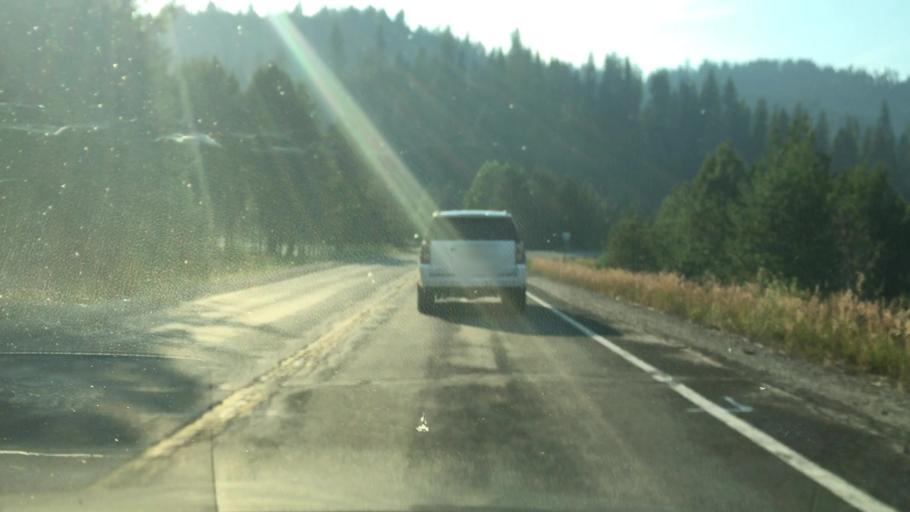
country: US
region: Idaho
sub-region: Valley County
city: Cascade
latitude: 44.2972
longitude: -116.0868
